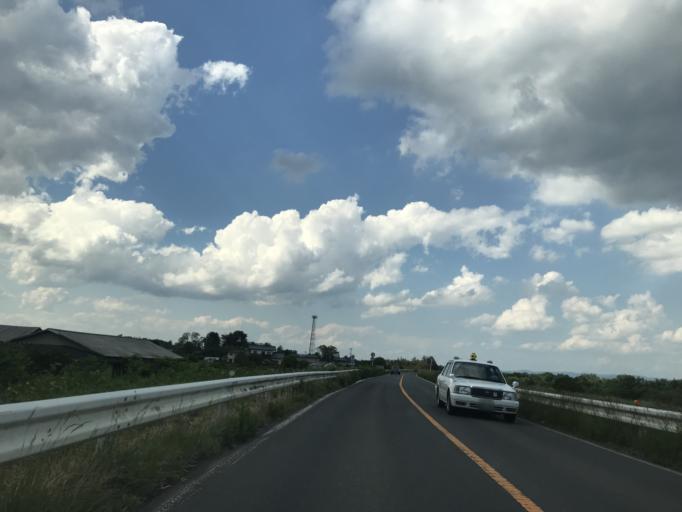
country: JP
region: Miyagi
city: Wakuya
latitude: 38.6366
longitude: 141.2045
